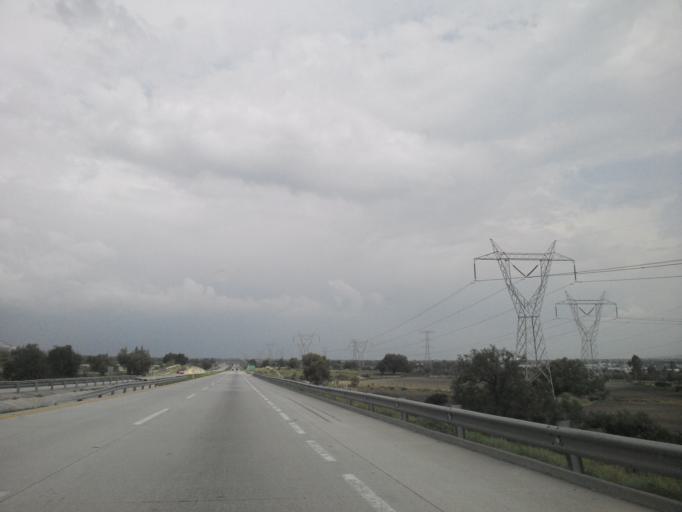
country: MX
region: Mexico
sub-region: Apaxco
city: Colonia Juarez
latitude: 20.0068
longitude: -99.1463
